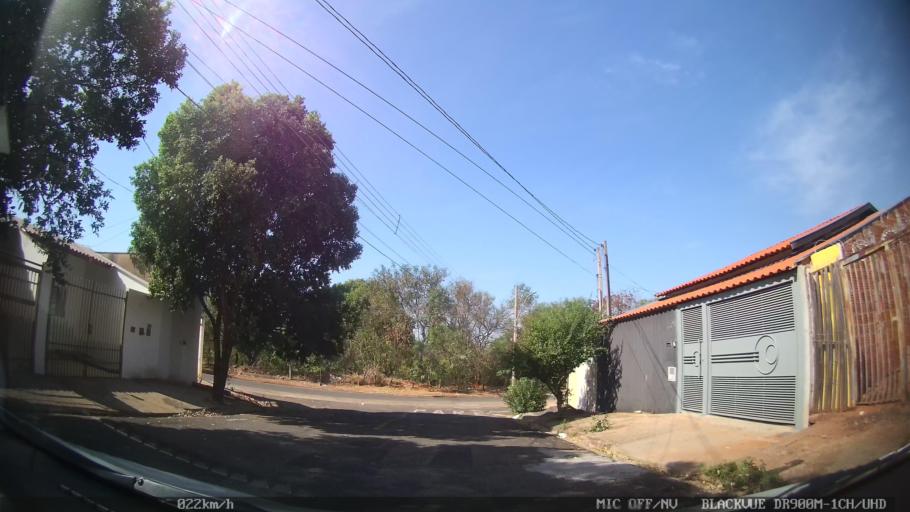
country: BR
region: Sao Paulo
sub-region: Sao Jose Do Rio Preto
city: Sao Jose do Rio Preto
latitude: -20.7882
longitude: -49.4370
